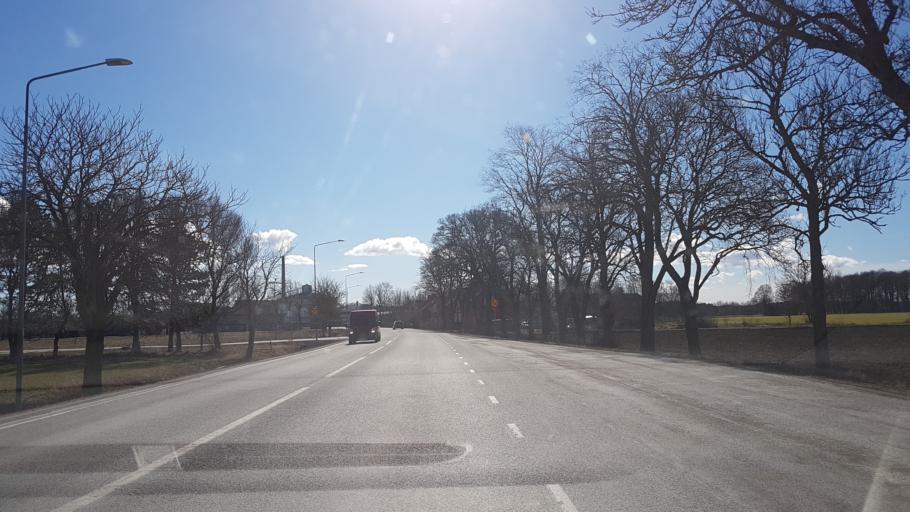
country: SE
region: Gotland
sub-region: Gotland
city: Visby
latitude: 57.5123
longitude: 18.4453
